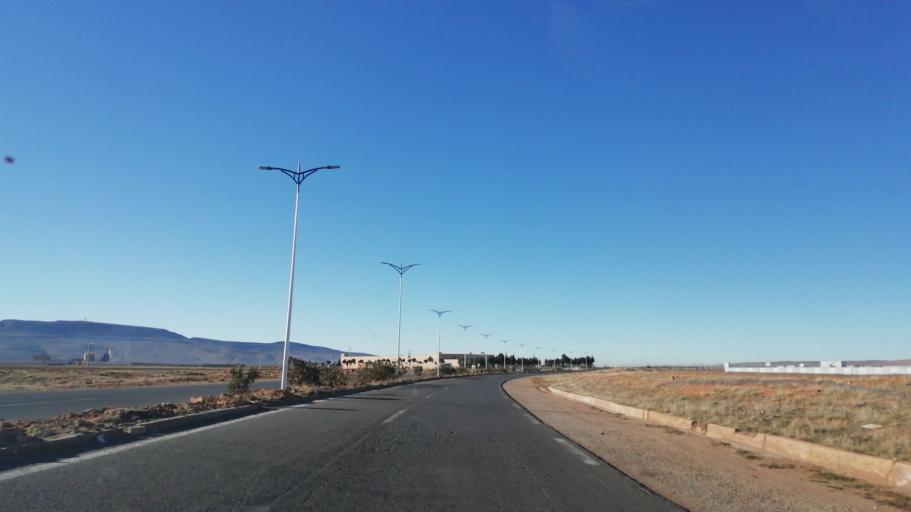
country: DZ
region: El Bayadh
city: El Bayadh
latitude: 33.6937
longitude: 1.0795
